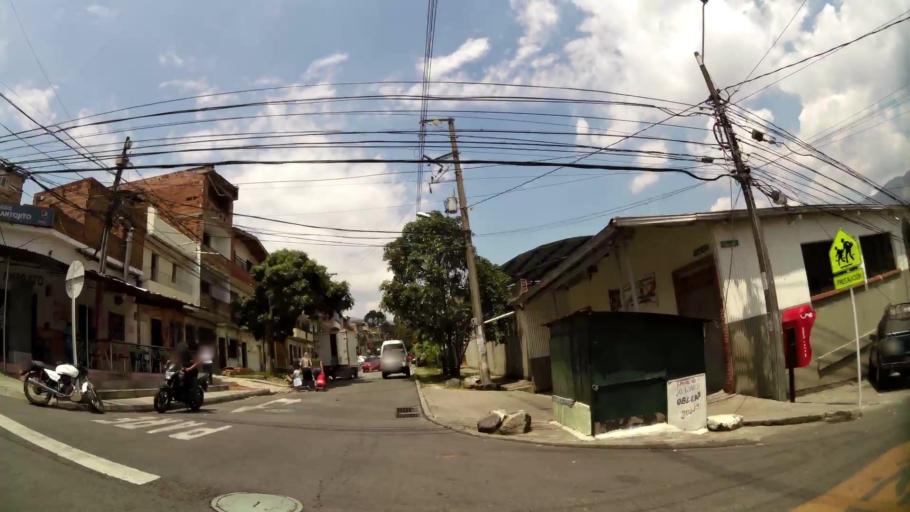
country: CO
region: Antioquia
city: Medellin
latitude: 6.2939
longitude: -75.5718
